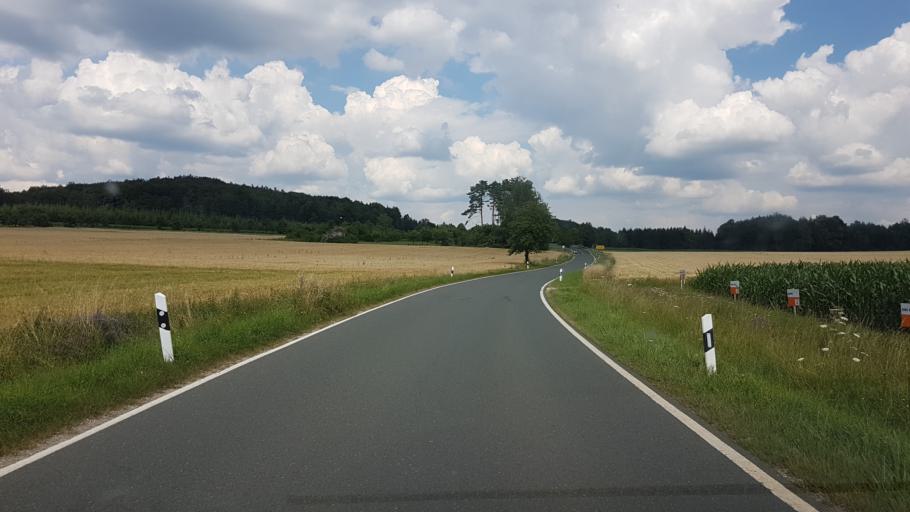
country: DE
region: Bavaria
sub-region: Upper Franconia
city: Egloffstein
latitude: 49.7620
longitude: 11.2676
